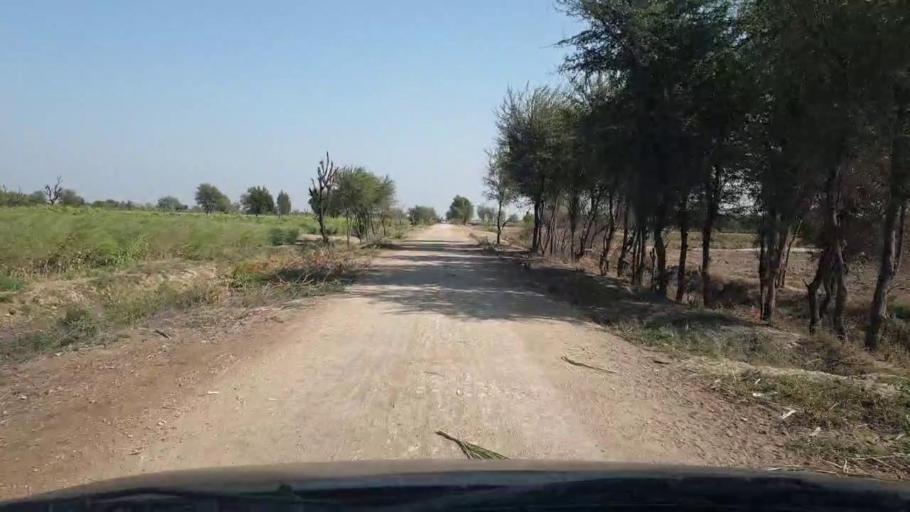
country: PK
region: Sindh
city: Samaro
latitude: 25.1918
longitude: 69.2849
